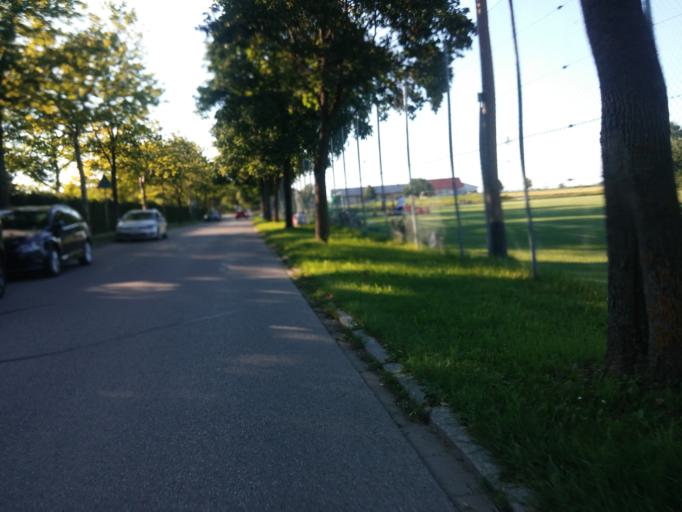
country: DE
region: Bavaria
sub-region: Upper Bavaria
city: Vaterstetten
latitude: 48.1096
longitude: 11.7847
